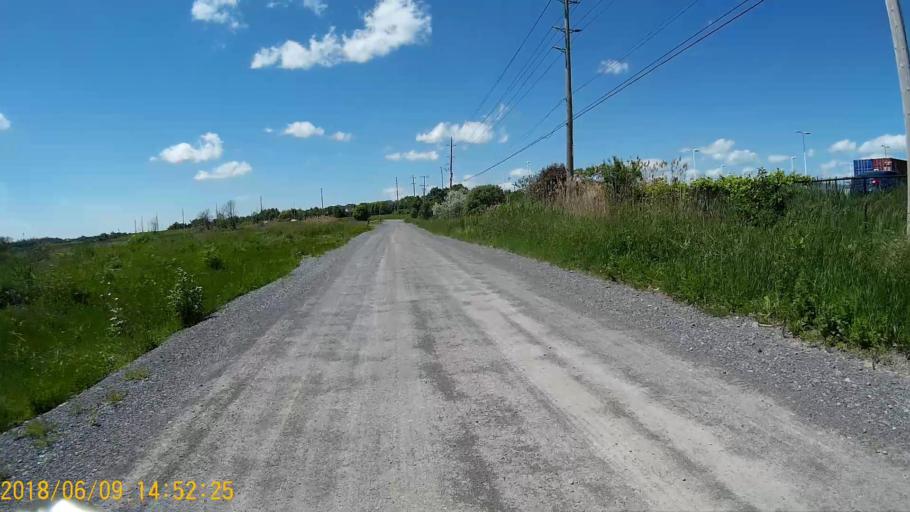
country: CA
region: Ontario
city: Bells Corners
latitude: 45.3080
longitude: -75.9206
